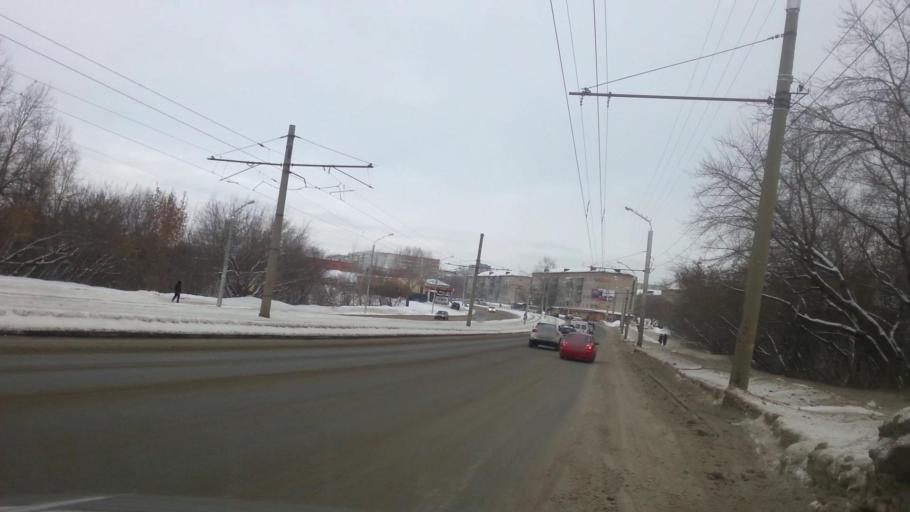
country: RU
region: Altai Krai
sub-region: Gorod Barnaulskiy
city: Barnaul
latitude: 53.3719
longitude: 83.7117
